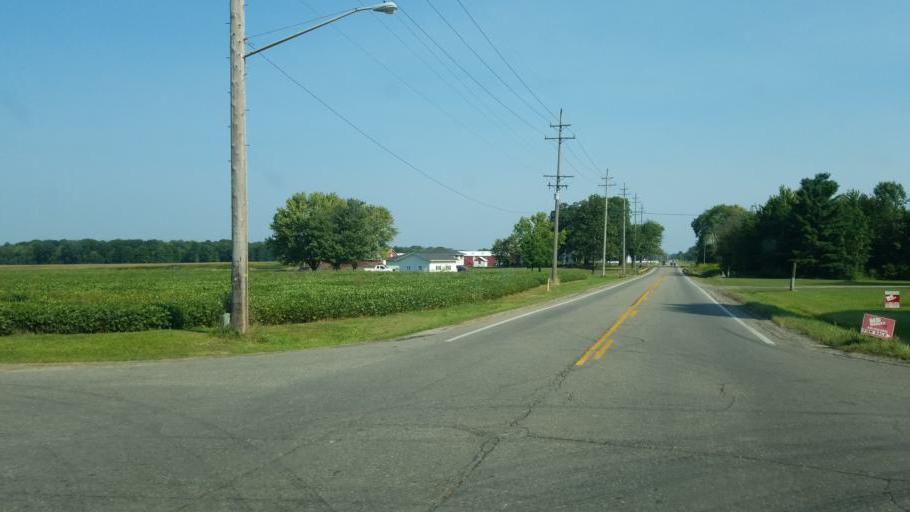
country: US
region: Ohio
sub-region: Ashtabula County
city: Orwell
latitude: 41.5495
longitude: -80.8668
